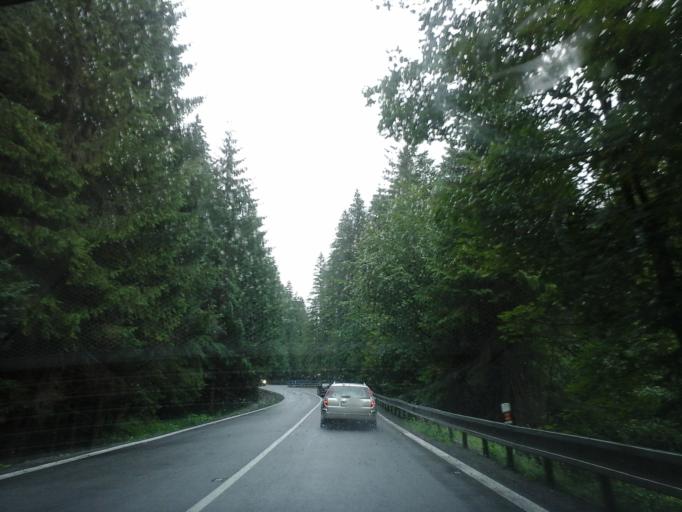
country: SK
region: Presovsky
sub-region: Okres Poprad
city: Poprad
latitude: 48.9375
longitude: 20.2859
